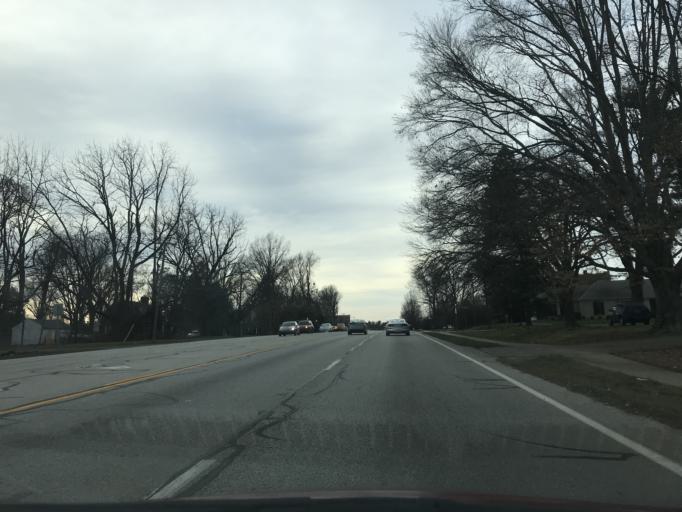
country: US
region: Kentucky
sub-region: Jefferson County
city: West Buechel
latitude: 38.1964
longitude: -85.6803
